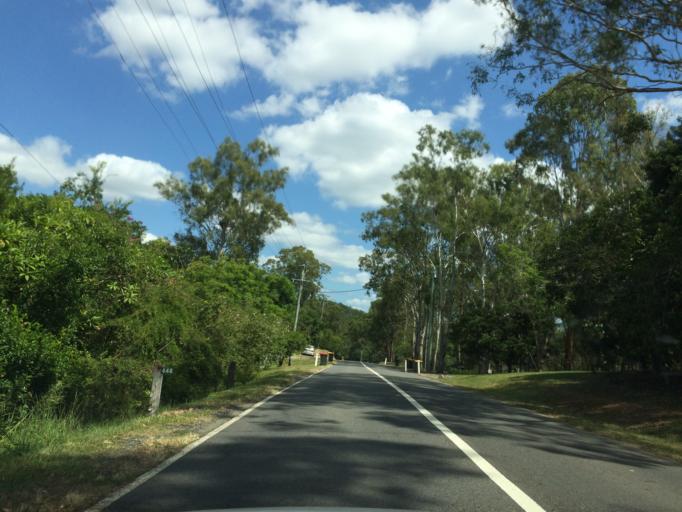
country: AU
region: Queensland
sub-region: Brisbane
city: Kenmore Hills
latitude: -27.4966
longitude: 152.9227
